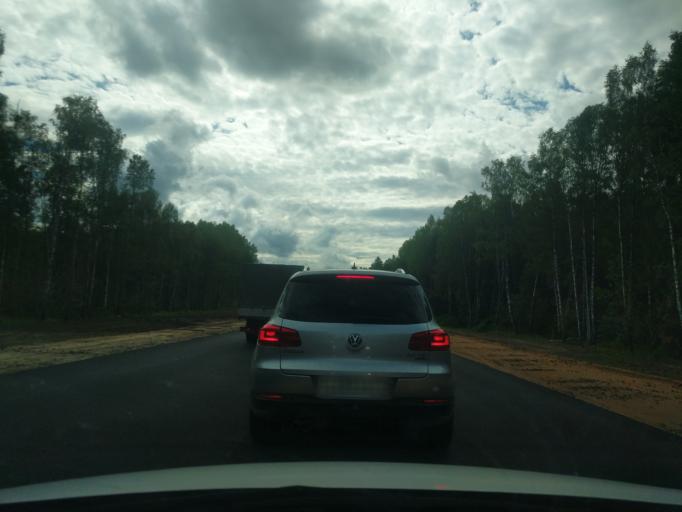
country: RU
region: Jaroslavl
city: Levashevo
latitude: 57.6850
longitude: 40.6036
